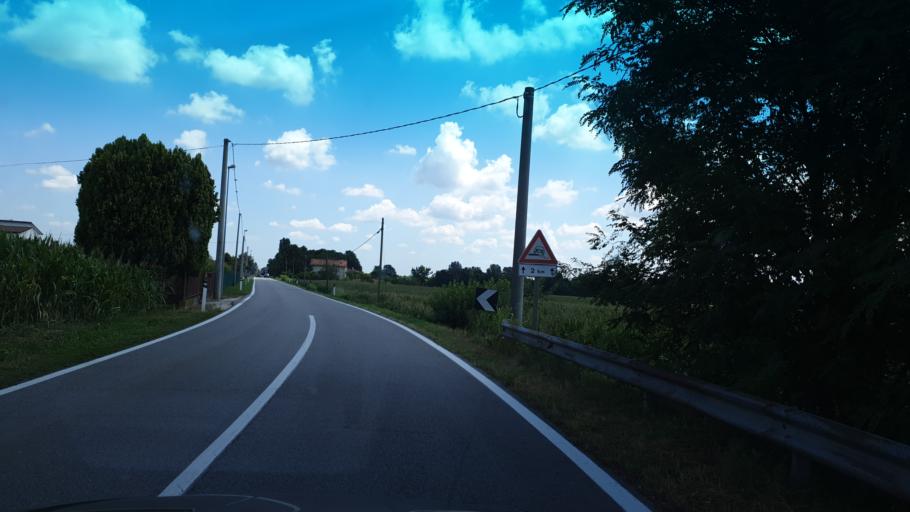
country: IT
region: Veneto
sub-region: Provincia di Padova
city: Stanghella
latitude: 45.1402
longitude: 11.7787
